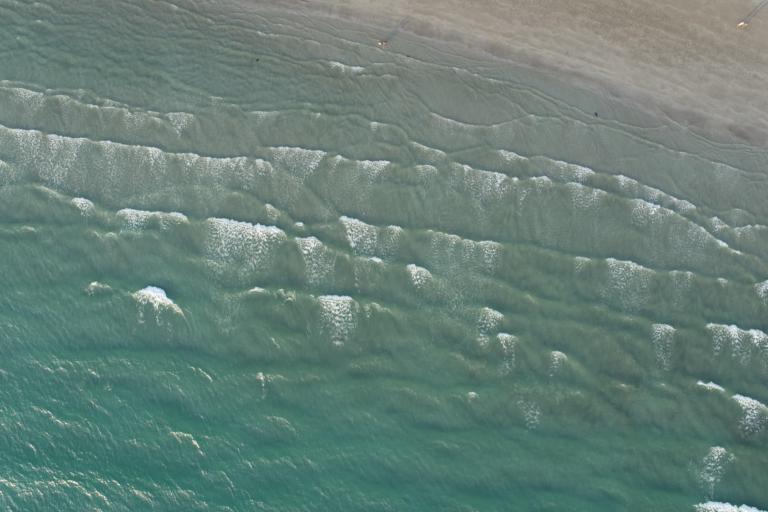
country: TH
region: Rayong
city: Rayong
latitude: 12.5937
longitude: 101.4122
